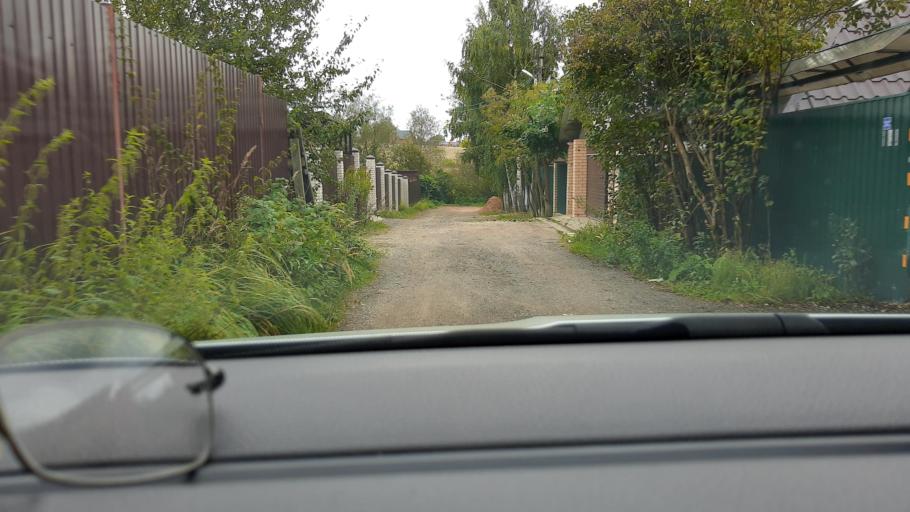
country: RU
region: Moscow
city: Vnukovo
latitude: 55.5909
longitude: 37.1935
